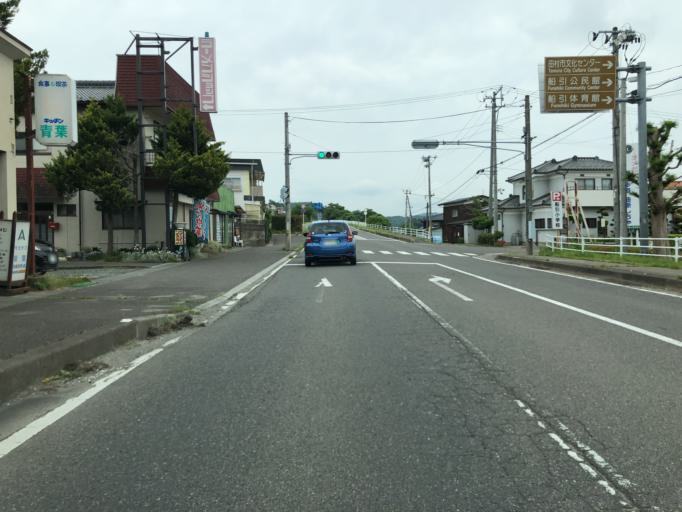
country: JP
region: Fukushima
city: Funehikimachi-funehiki
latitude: 37.4367
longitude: 140.5817
